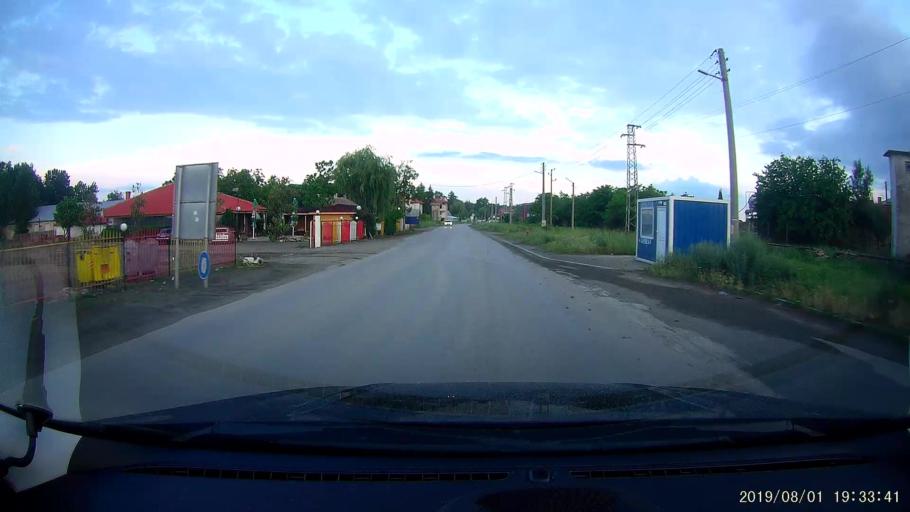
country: BG
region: Burgas
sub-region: Obshtina Sungurlare
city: Sungurlare
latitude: 42.7766
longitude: 26.8772
